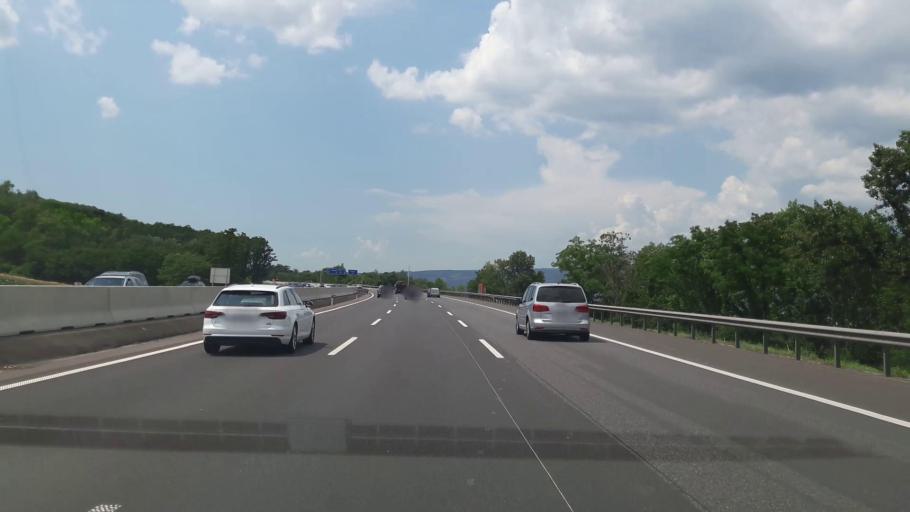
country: AT
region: Lower Austria
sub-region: Politischer Bezirk Melk
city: Klein-Poechlarn
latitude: 48.1987
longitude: 15.2374
